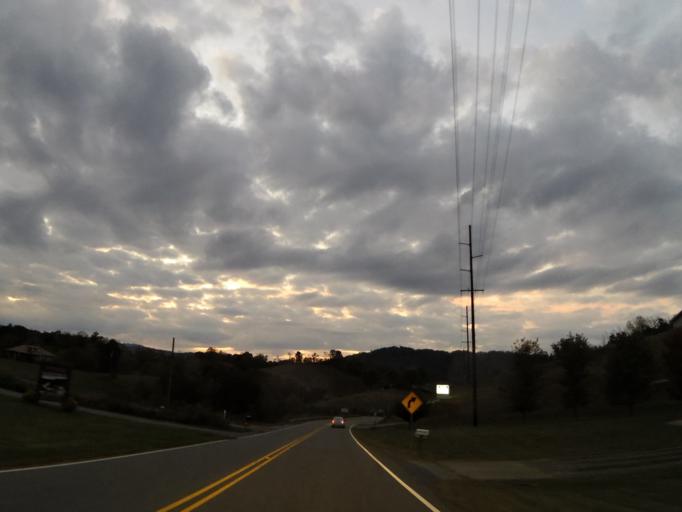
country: US
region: North Carolina
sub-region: Madison County
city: Marshall
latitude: 35.8164
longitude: -82.7001
